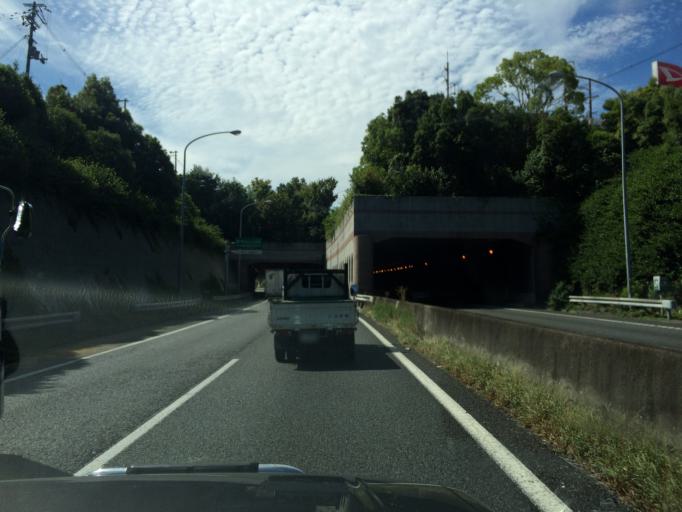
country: JP
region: Osaka
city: Izumi
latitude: 34.4916
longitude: 135.4676
